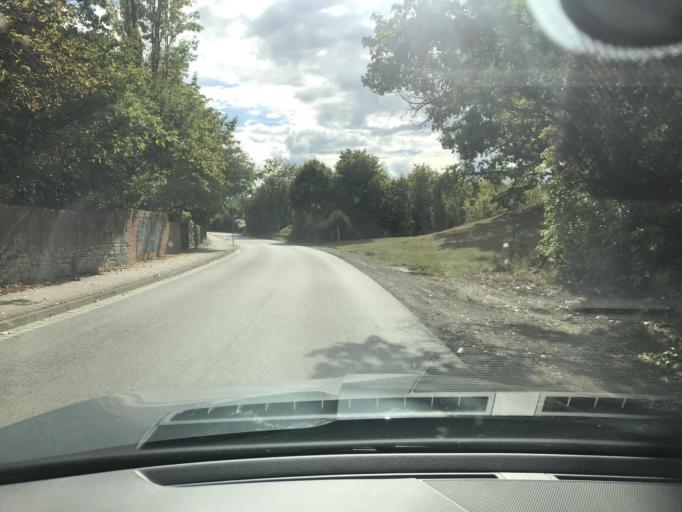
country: DE
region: Saxony-Anhalt
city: Quedlinburg
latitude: 51.7744
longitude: 11.1421
